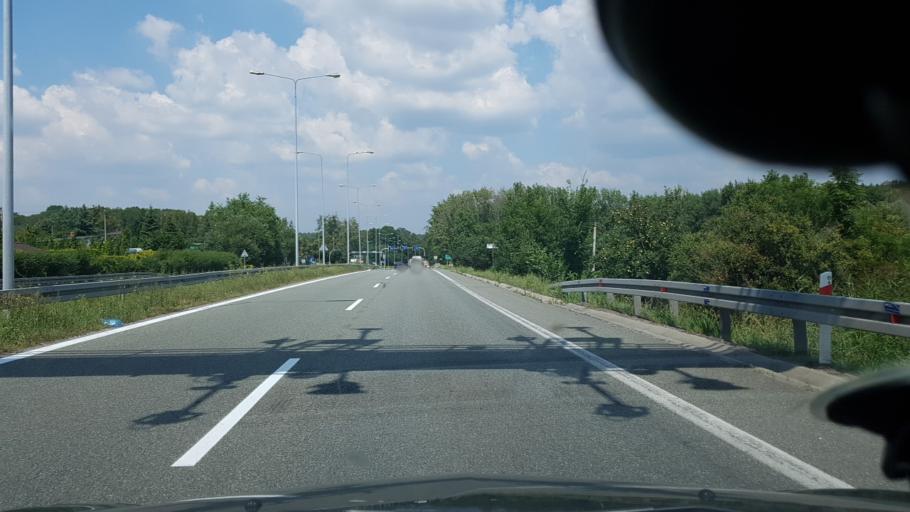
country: PL
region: Silesian Voivodeship
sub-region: Powiat mikolowski
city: Laziska Gorne
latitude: 50.1555
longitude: 18.8493
